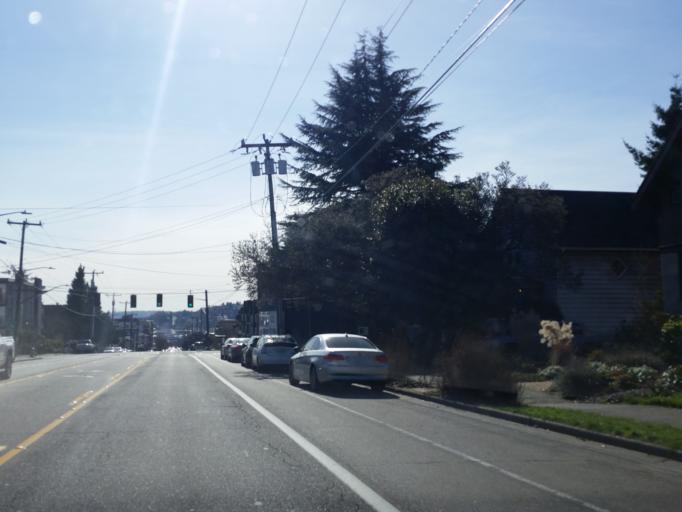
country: US
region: Washington
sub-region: King County
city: Shoreline
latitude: 47.6802
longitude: -122.3876
